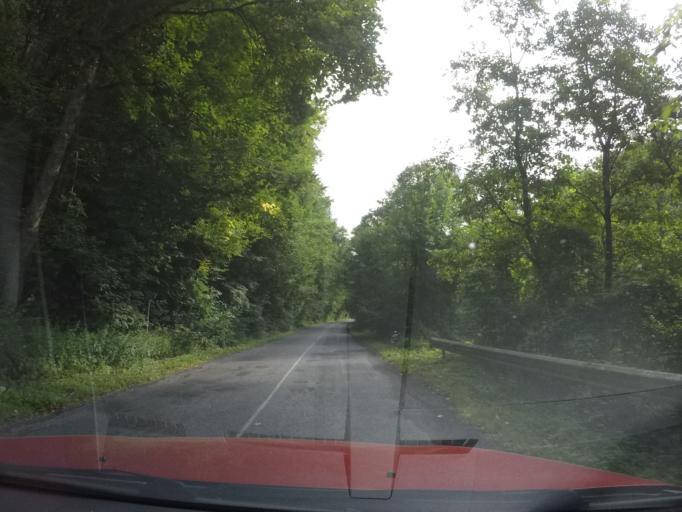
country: UA
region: Zakarpattia
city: Velykyi Bereznyi
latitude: 48.9432
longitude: 22.4920
